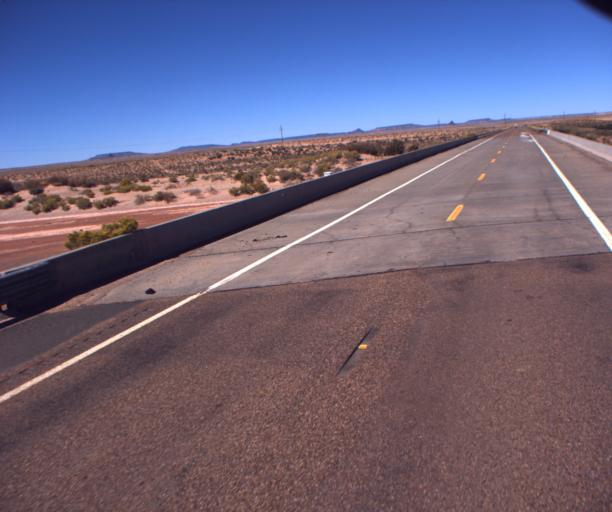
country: US
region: Arizona
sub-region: Navajo County
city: Holbrook
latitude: 35.0626
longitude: -110.0975
